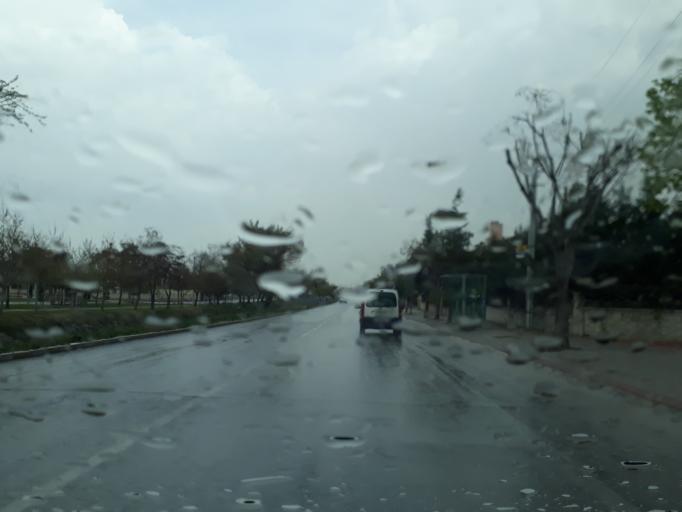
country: TR
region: Konya
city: Selcuklu
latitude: 37.9182
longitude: 32.4821
